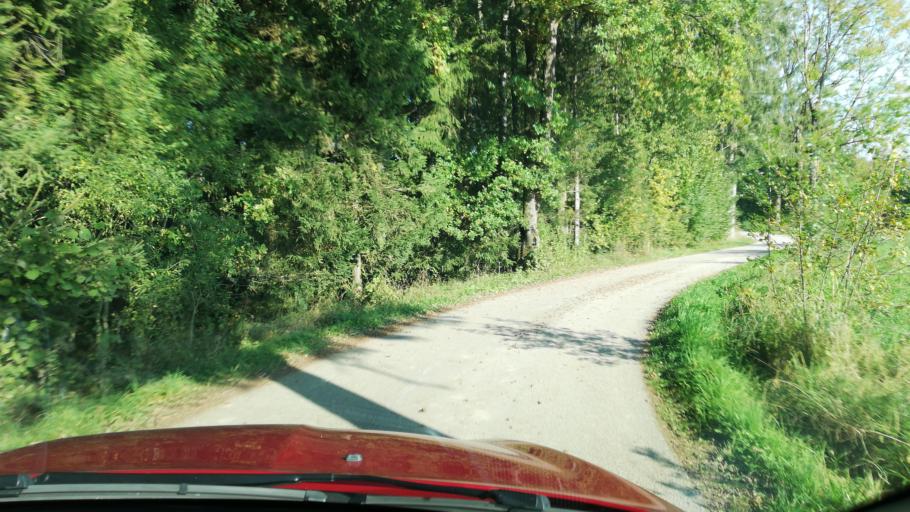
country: AT
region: Upper Austria
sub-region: Politischer Bezirk Kirchdorf an der Krems
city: Kremsmunster
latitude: 48.1000
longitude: 14.1572
